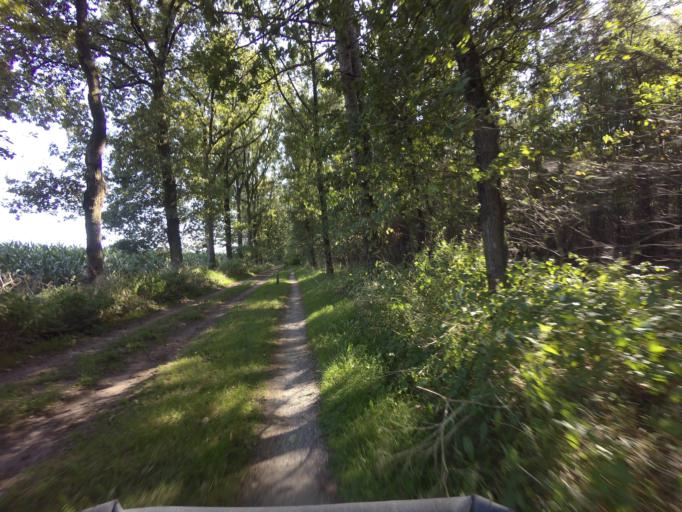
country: NL
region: Drenthe
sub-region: Gemeente Tynaarlo
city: Vries
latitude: 53.0776
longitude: 6.5179
